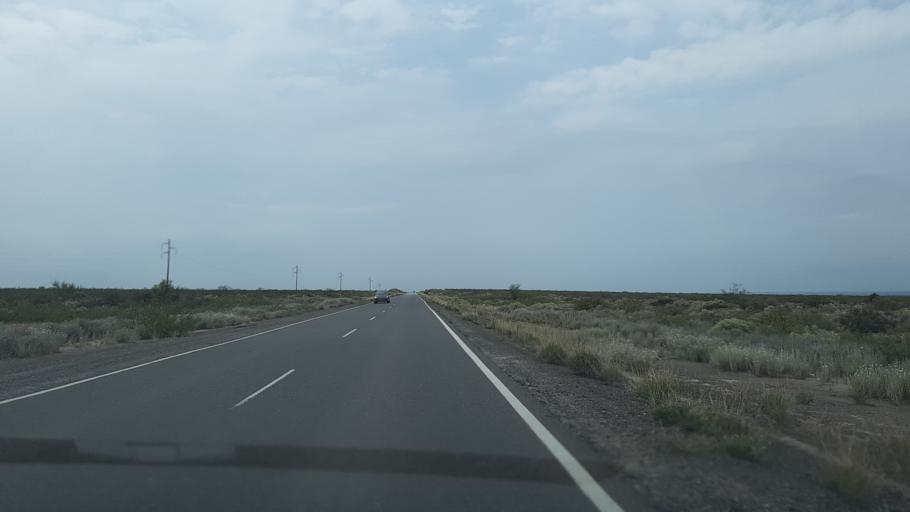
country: AR
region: Rio Negro
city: Catriel
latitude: -38.1647
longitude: -67.9497
